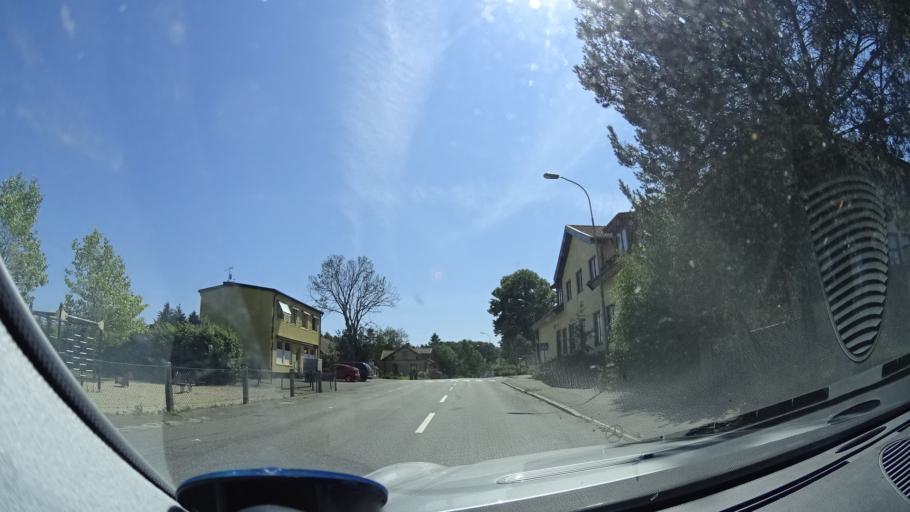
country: SE
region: Skane
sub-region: Kristianstads Kommun
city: Degeberga
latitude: 55.8858
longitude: 14.0174
